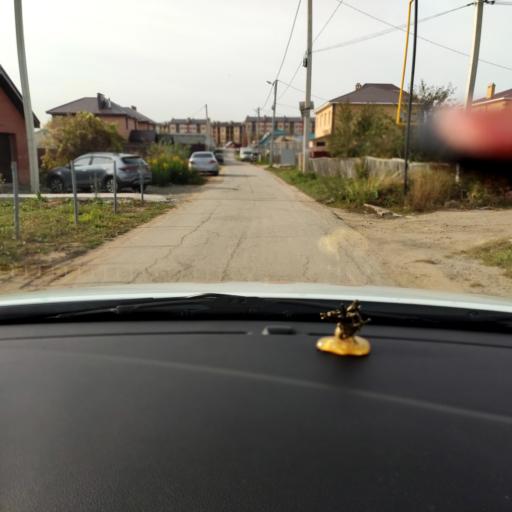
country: RU
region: Tatarstan
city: Vysokaya Gora
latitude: 55.9132
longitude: 49.2987
